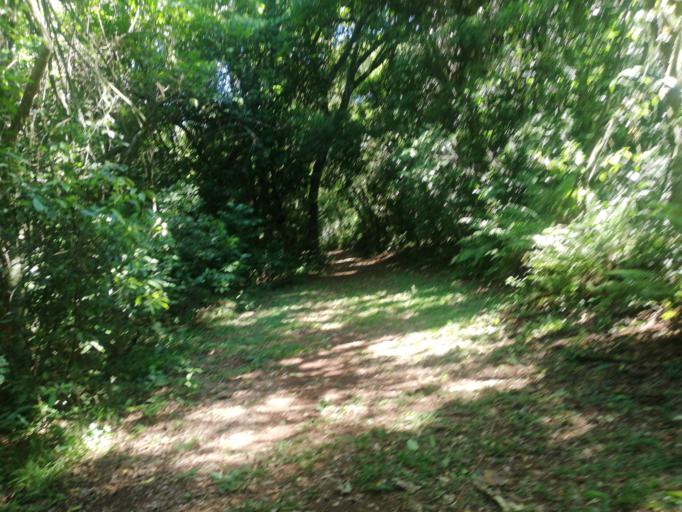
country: AR
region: Misiones
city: Cerro Azul
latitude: -27.7480
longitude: -55.5610
